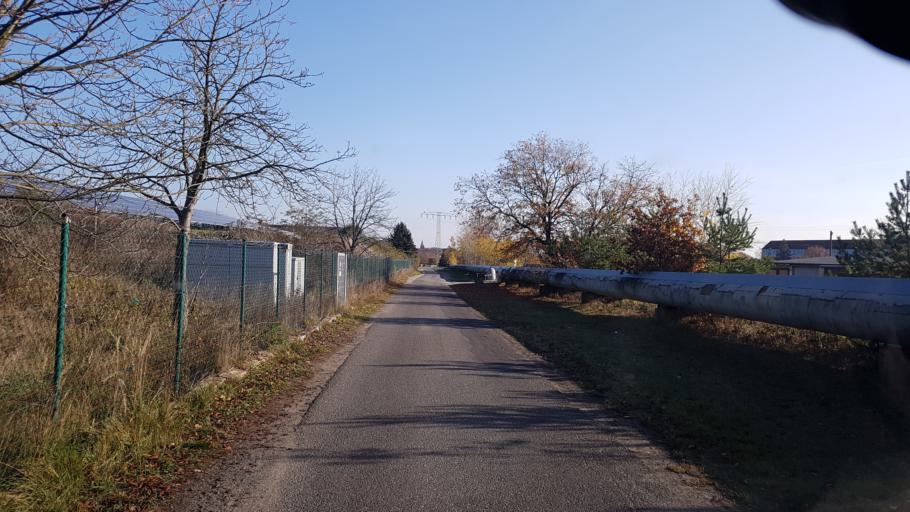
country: DE
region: Brandenburg
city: Grossraschen
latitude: 51.5919
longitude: 13.9939
